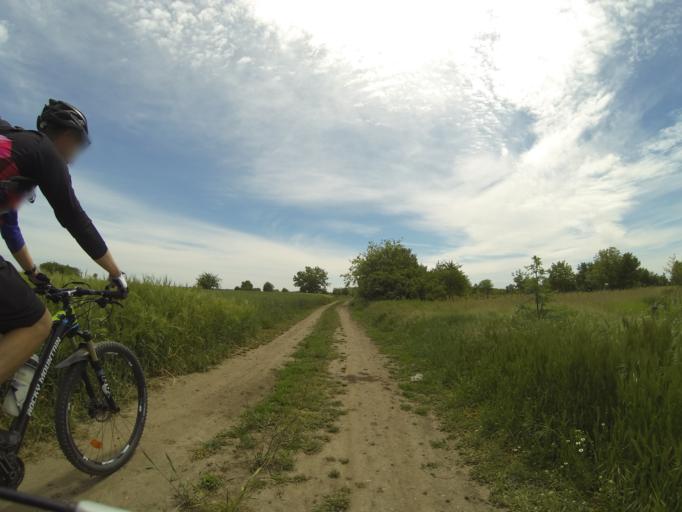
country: RO
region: Dolj
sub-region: Comuna Leu
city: Leu
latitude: 44.2004
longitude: 24.0010
